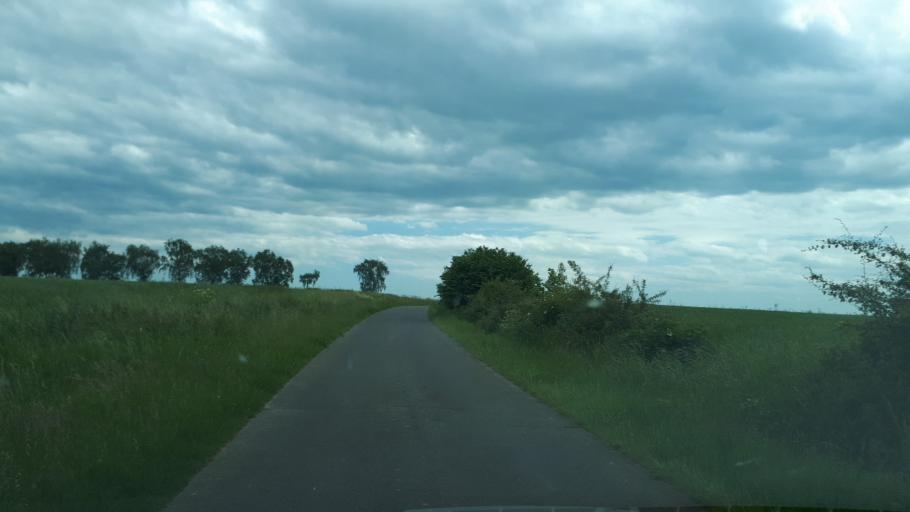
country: DE
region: Rheinland-Pfalz
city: Greimersburg
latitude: 50.1916
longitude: 7.1328
